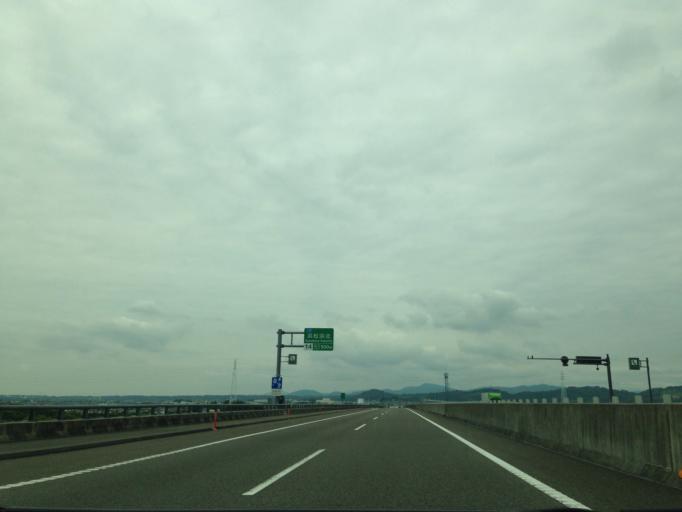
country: JP
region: Shizuoka
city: Hamakita
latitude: 34.8327
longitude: 137.8274
